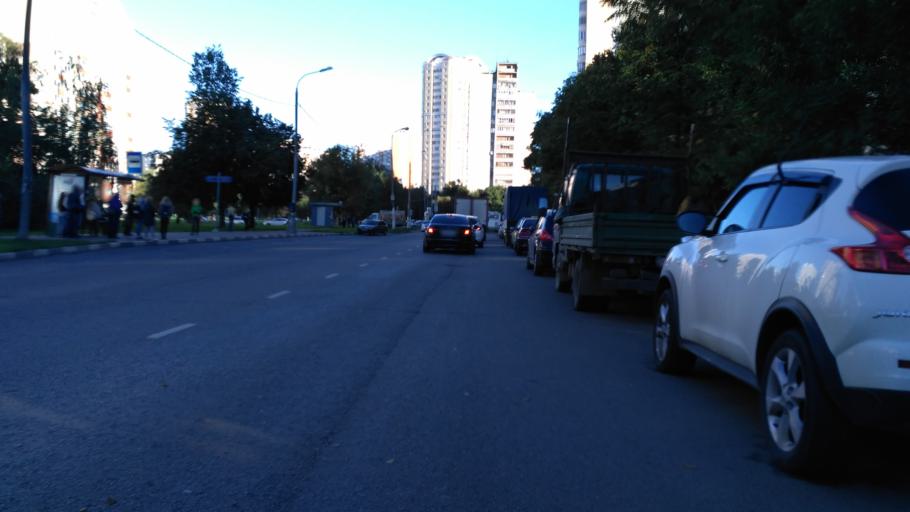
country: RU
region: Moskovskaya
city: Vostochnoe Degunino
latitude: 55.8709
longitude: 37.5553
